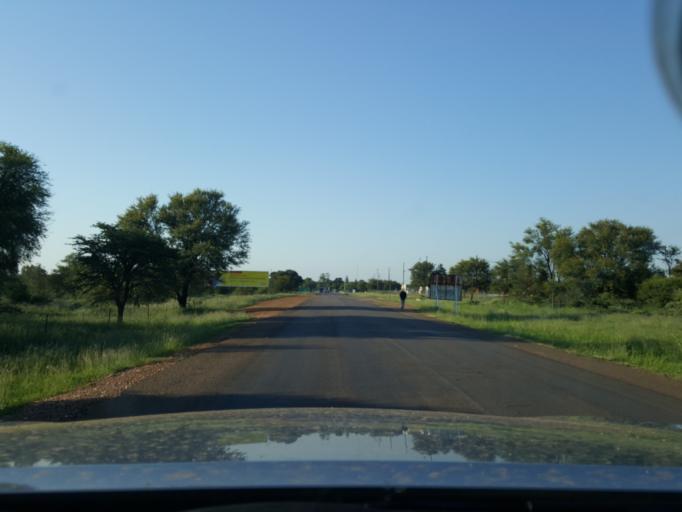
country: BW
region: South East
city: Janeng
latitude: -25.6333
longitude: 25.5742
